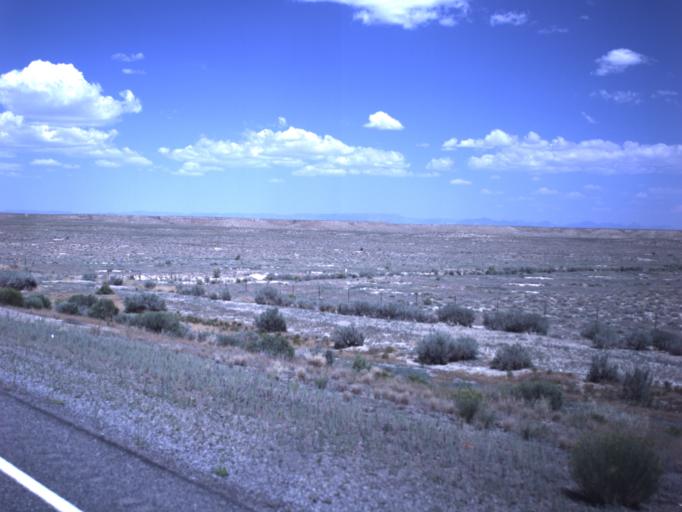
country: US
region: Utah
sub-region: Emery County
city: Huntington
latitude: 39.3674
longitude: -110.9203
